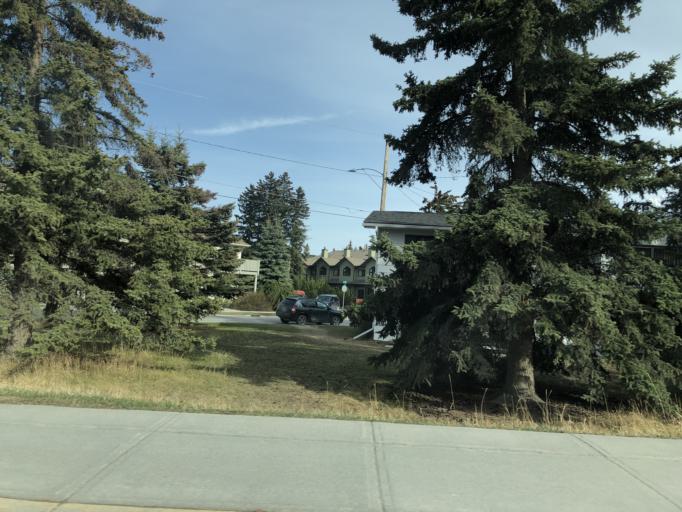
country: CA
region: Alberta
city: Canmore
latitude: 51.0867
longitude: -115.3638
